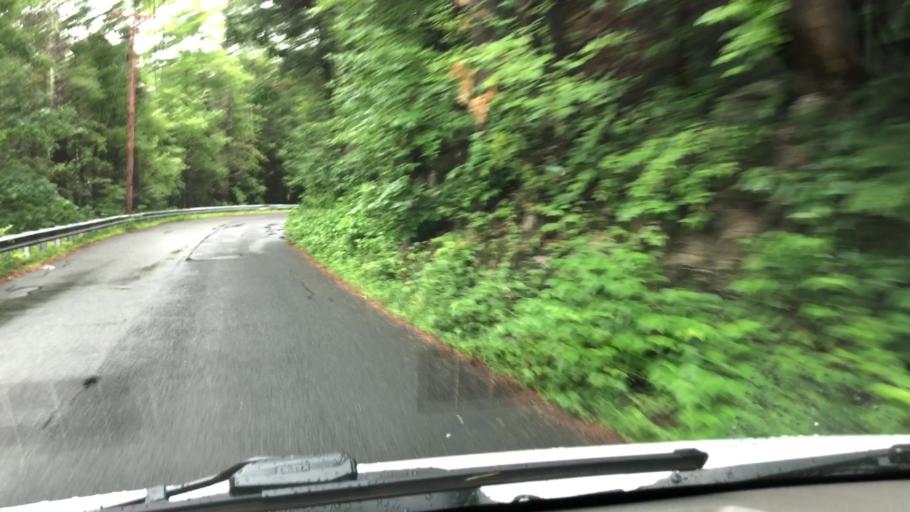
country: US
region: Massachusetts
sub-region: Hampshire County
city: Williamsburg
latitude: 42.3611
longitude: -72.7024
